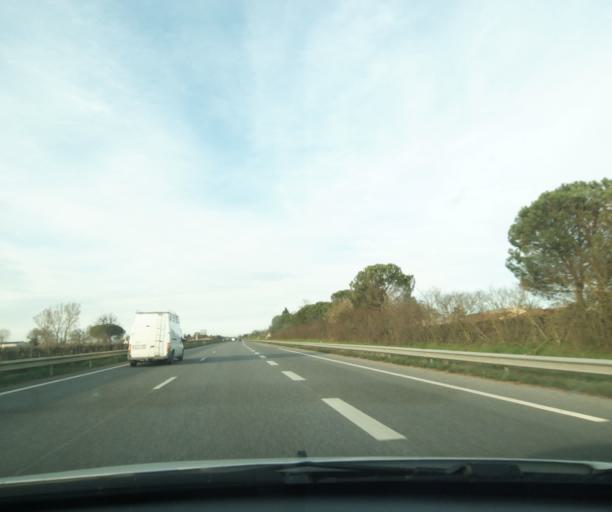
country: FR
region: Midi-Pyrenees
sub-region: Departement de la Haute-Garonne
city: Le Fauga
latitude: 43.3991
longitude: 1.2895
